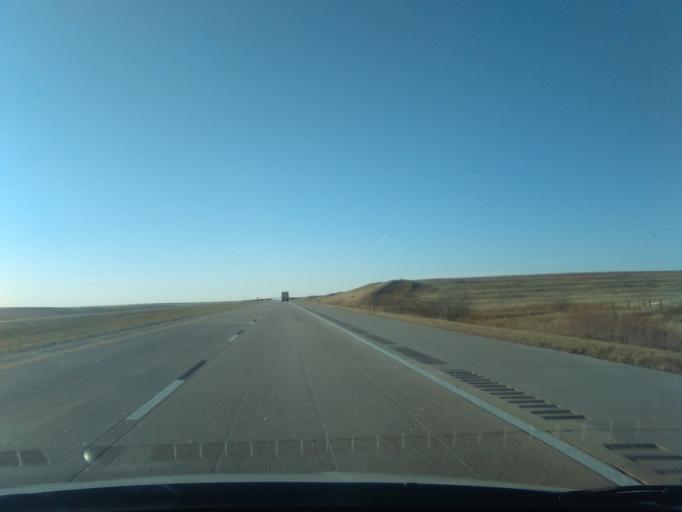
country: US
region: Nebraska
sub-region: Deuel County
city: Chappell
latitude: 41.1134
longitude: -102.6903
